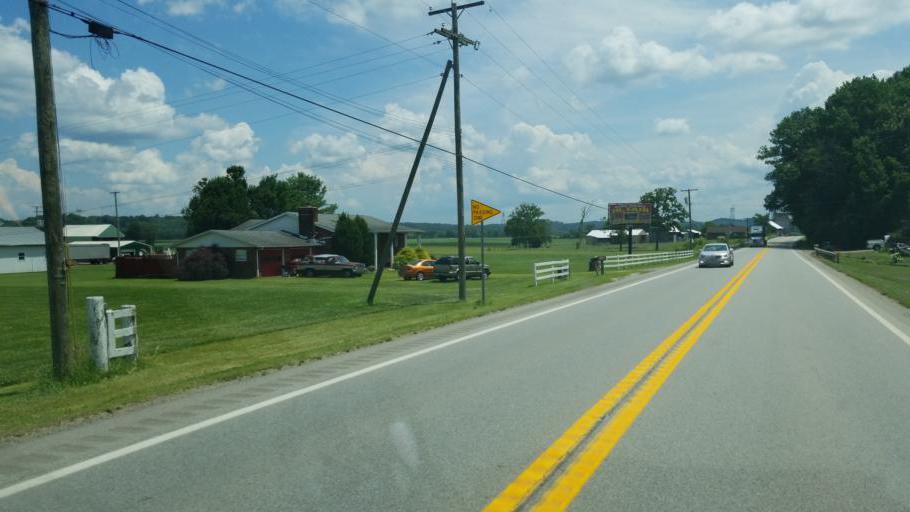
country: US
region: West Virginia
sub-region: Putnam County
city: Buffalo
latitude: 38.7557
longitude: -81.9906
